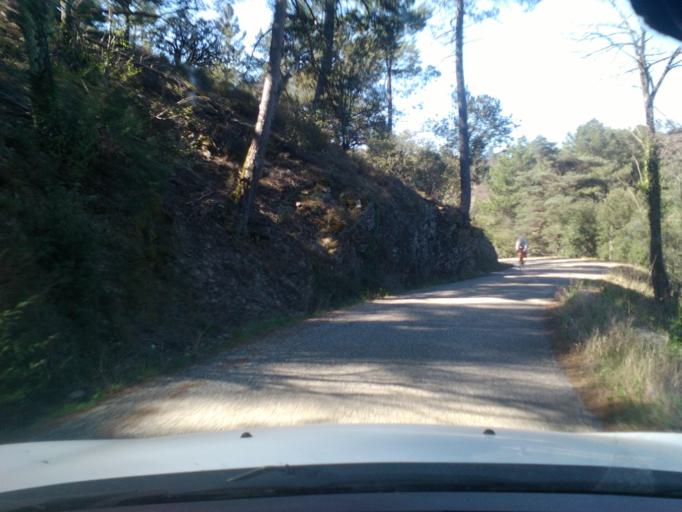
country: FR
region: Languedoc-Roussillon
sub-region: Departement du Gard
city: Valleraugue
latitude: 44.1336
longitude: 3.7573
